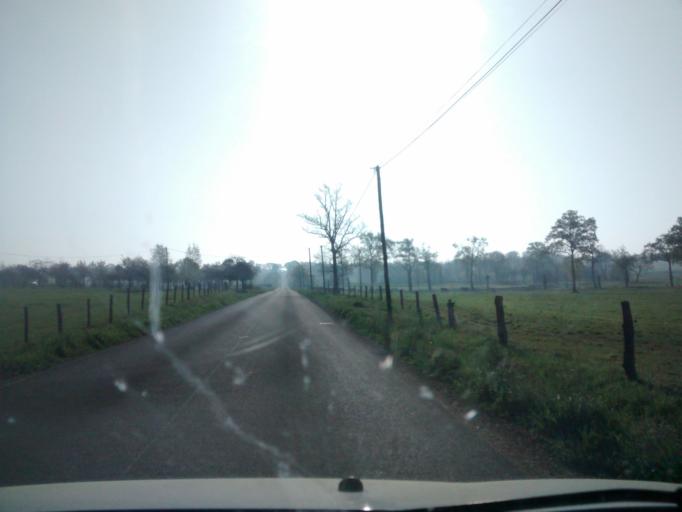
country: FR
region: Brittany
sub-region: Departement d'Ille-et-Vilaine
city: Saint-Jean-sur-Couesnon
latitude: 48.2778
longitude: -1.3514
